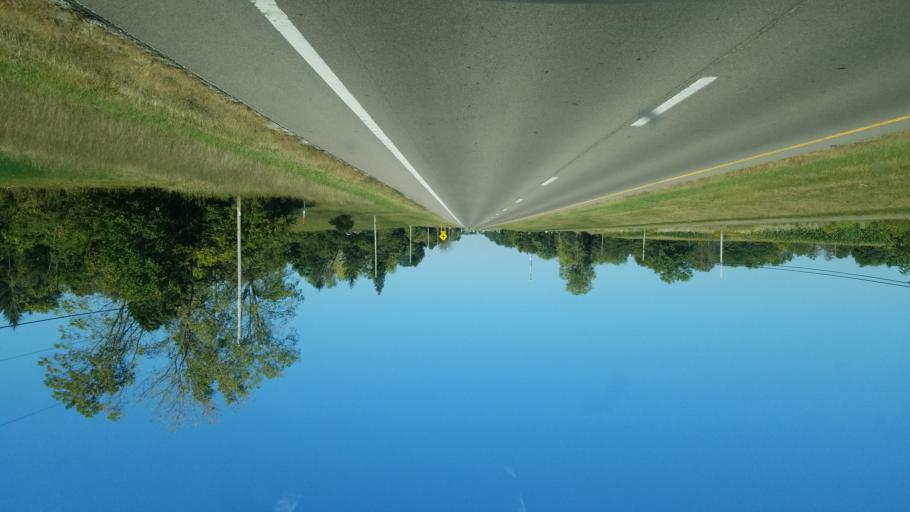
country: US
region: Ohio
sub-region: Clark County
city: Lisbon
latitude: 39.9258
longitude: -83.6512
